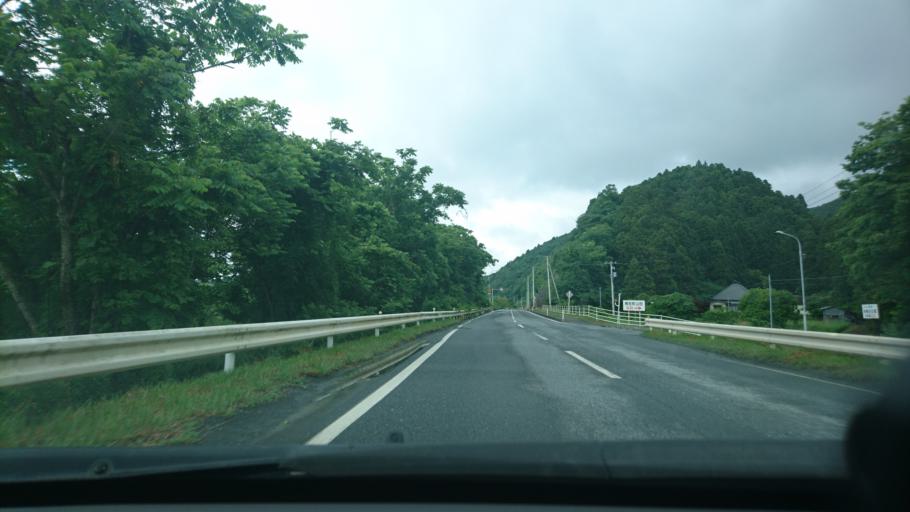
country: JP
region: Miyagi
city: Ishinomaki
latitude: 38.5650
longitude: 141.3000
